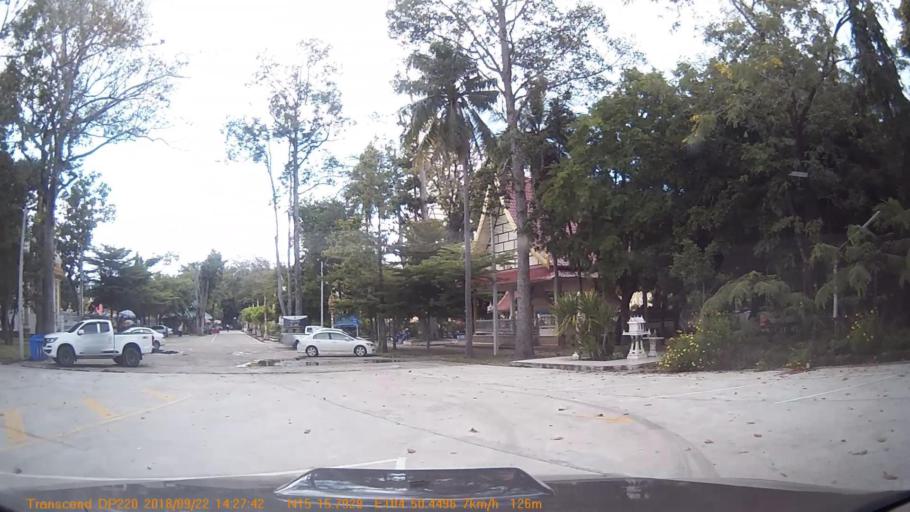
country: TH
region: Changwat Ubon Ratchathani
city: Ubon Ratchathani
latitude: 15.2632
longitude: 104.8408
